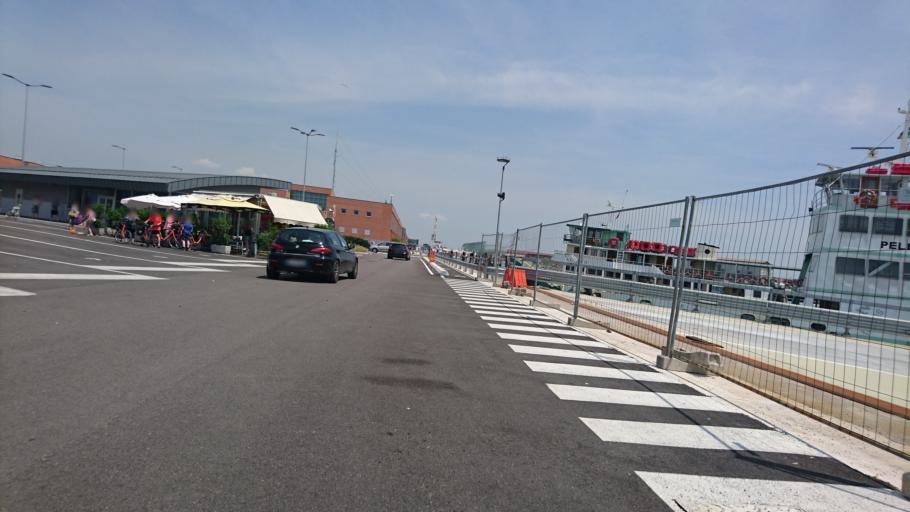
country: IT
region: Veneto
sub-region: Provincia di Venezia
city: Giudecca
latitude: 45.4384
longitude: 12.3044
